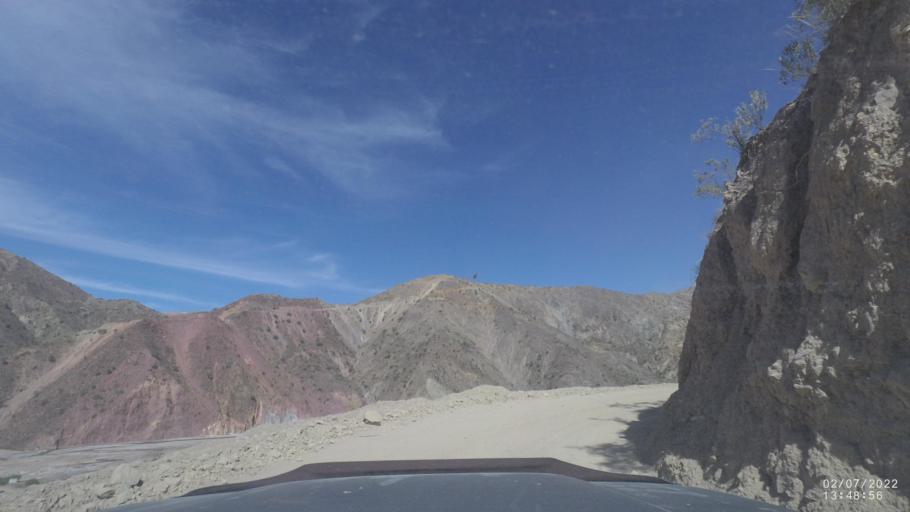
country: BO
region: Cochabamba
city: Irpa Irpa
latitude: -17.8187
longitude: -66.3738
